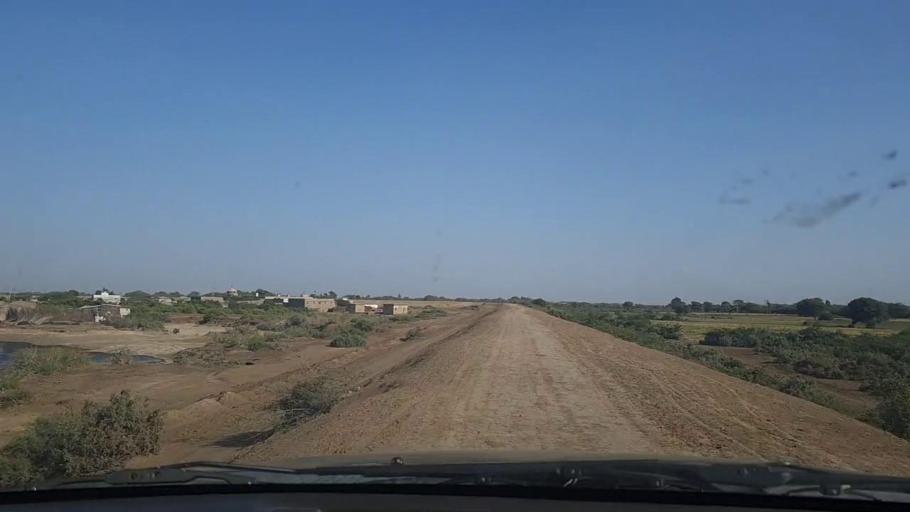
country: PK
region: Sindh
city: Chuhar Jamali
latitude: 24.3692
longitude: 67.7745
